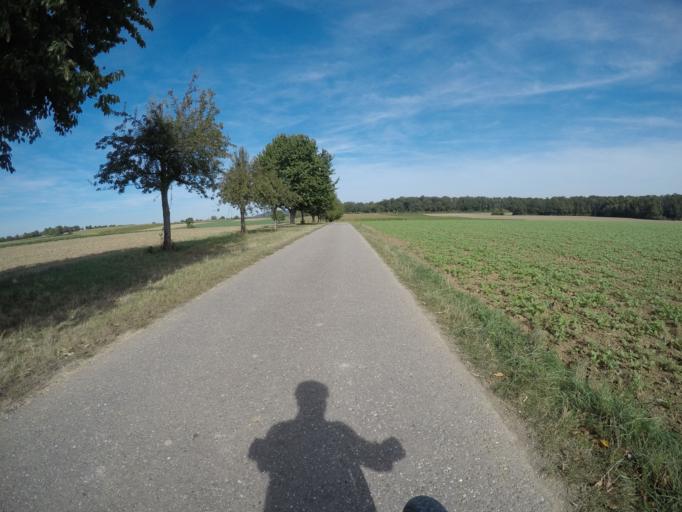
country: DE
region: Baden-Wuerttemberg
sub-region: Regierungsbezirk Stuttgart
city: Oberriexingen
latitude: 48.9453
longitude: 9.0271
